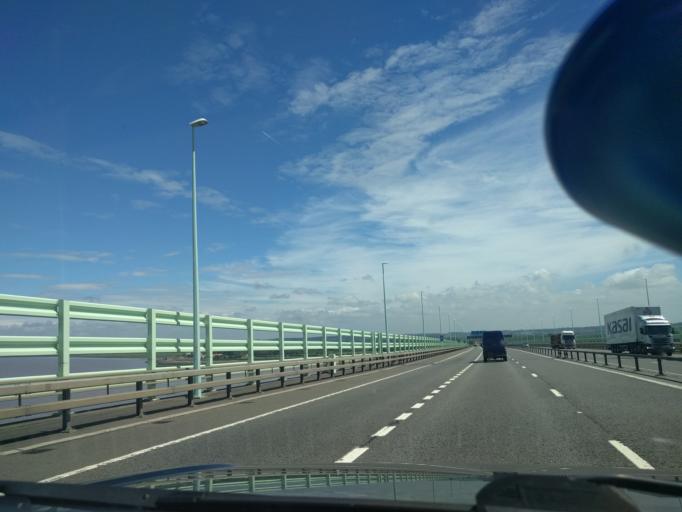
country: GB
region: England
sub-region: South Gloucestershire
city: Severn Beach
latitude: 51.5698
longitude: -2.6739
